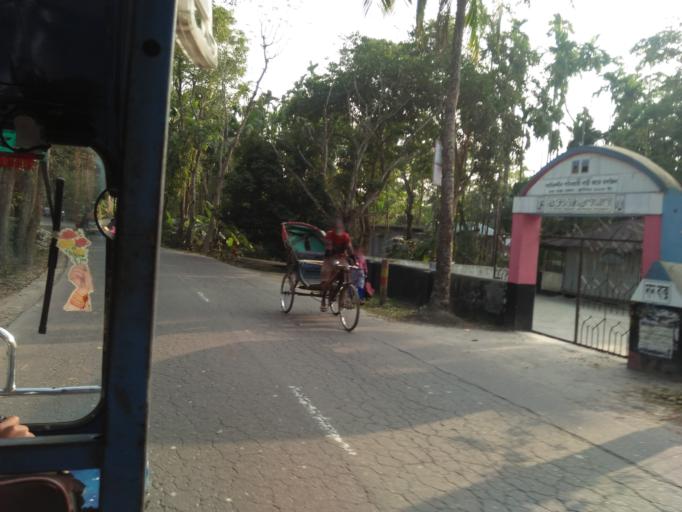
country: BD
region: Barisal
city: Bhola
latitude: 22.7053
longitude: 90.6402
